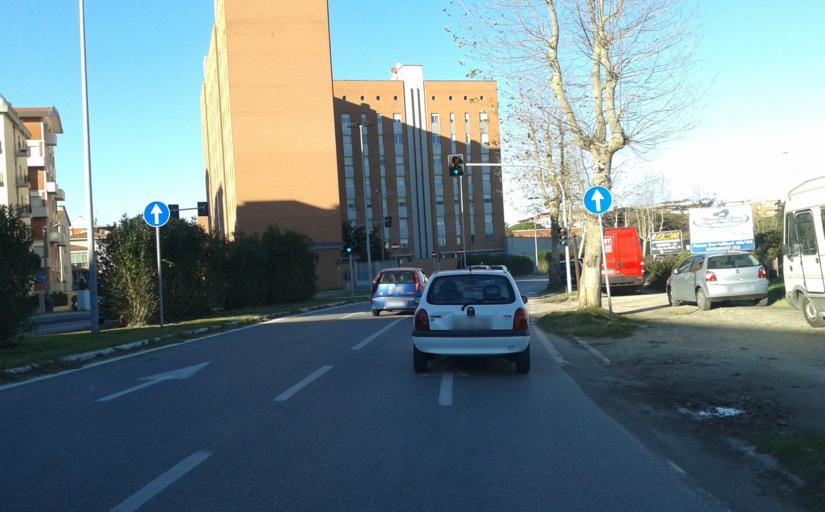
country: IT
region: Tuscany
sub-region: Provincia di Livorno
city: Livorno
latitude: 43.5375
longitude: 10.3227
